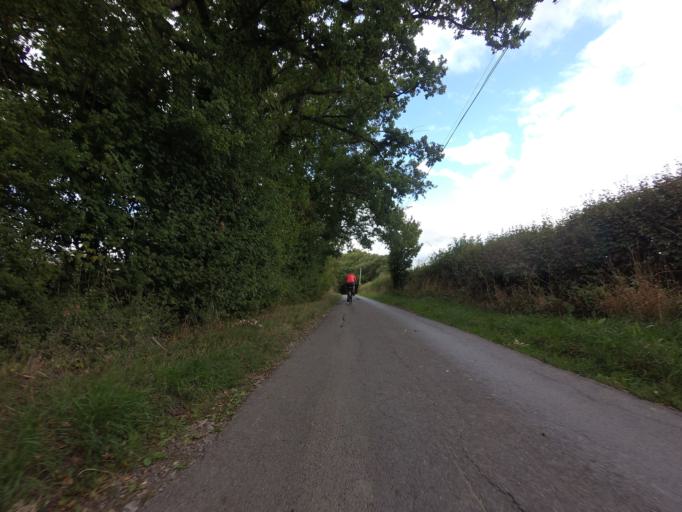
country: GB
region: England
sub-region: Kent
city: Staplehurst
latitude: 51.2106
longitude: 0.5448
